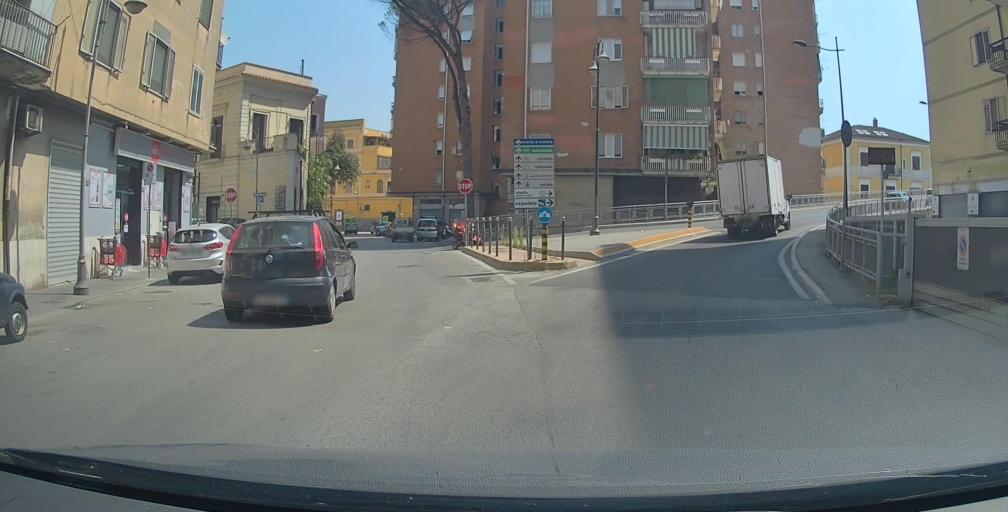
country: IT
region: Campania
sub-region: Provincia di Salerno
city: Nocera Inferiore
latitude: 40.7451
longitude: 14.6467
